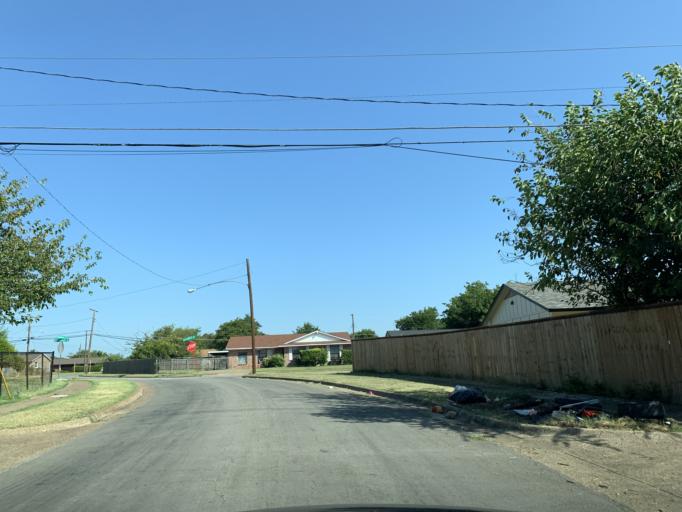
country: US
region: Texas
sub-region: Dallas County
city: Hutchins
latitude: 32.6653
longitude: -96.7619
